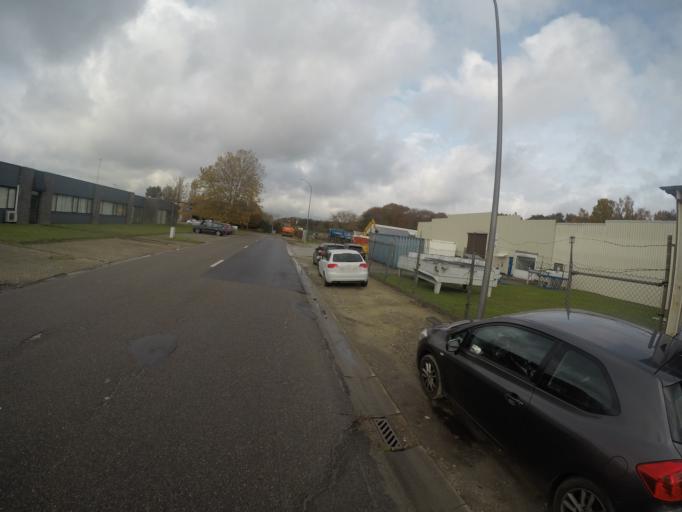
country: BE
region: Flanders
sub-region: Provincie Oost-Vlaanderen
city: Sint-Niklaas
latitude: 51.1424
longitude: 4.1556
